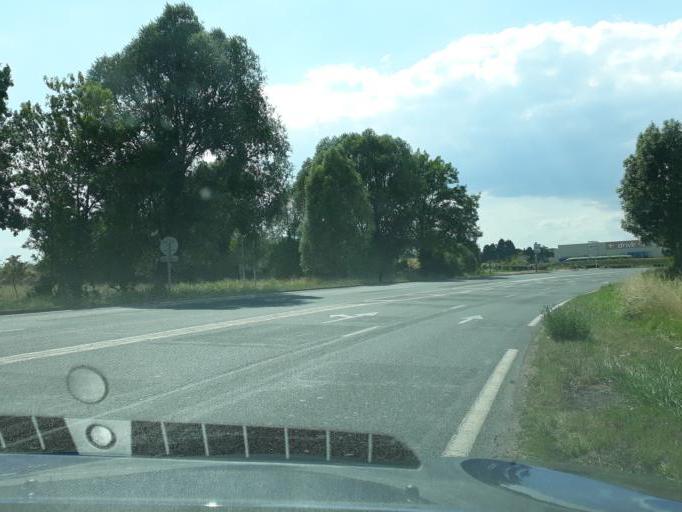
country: FR
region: Bourgogne
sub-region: Departement de la Nievre
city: Marzy
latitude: 46.9954
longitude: 3.1147
